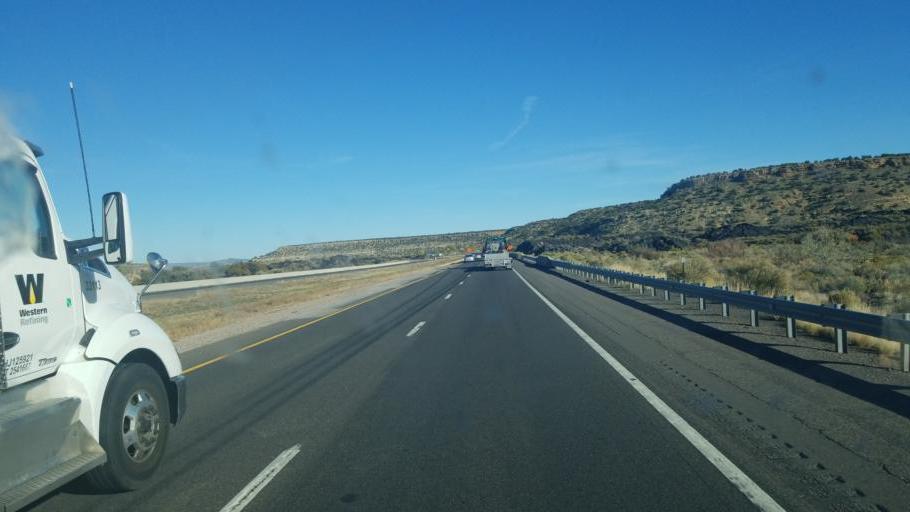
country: US
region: New Mexico
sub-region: Cibola County
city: Skyline-Ganipa
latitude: 35.0635
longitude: -107.7083
